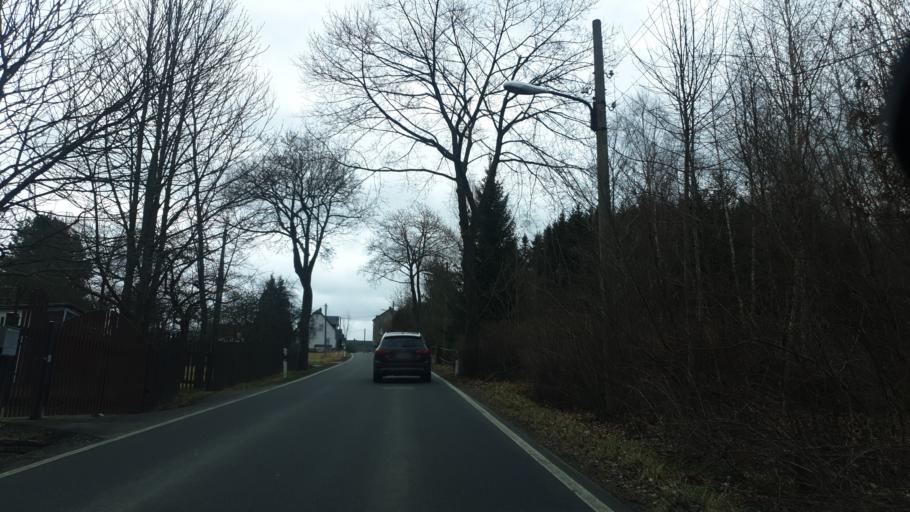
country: DE
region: Saxony
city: Bad Elster
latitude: 50.2755
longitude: 12.2635
